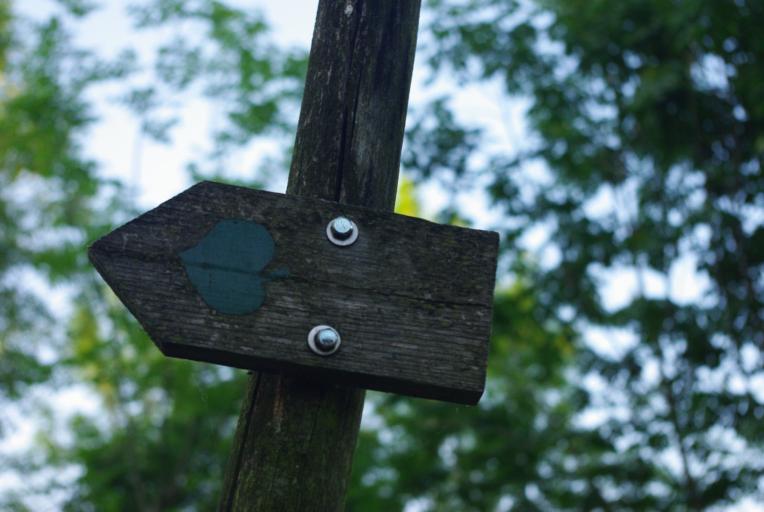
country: HU
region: Pest
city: Pilisszentivan
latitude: 47.6094
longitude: 18.8682
